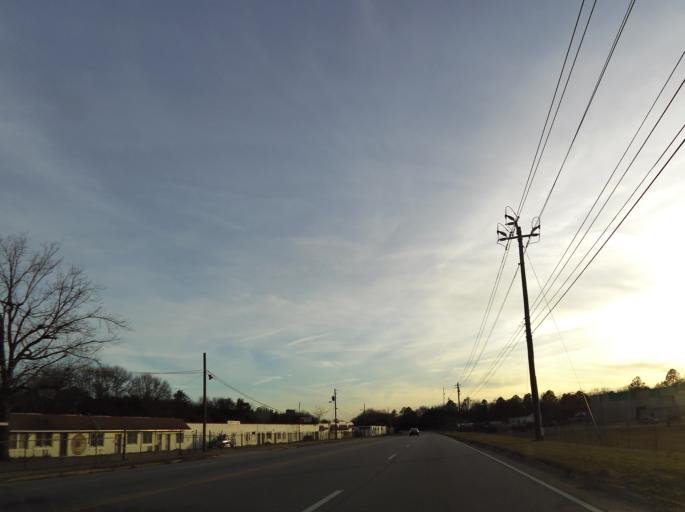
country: US
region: Georgia
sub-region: Bibb County
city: Macon
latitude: 32.7909
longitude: -83.6504
